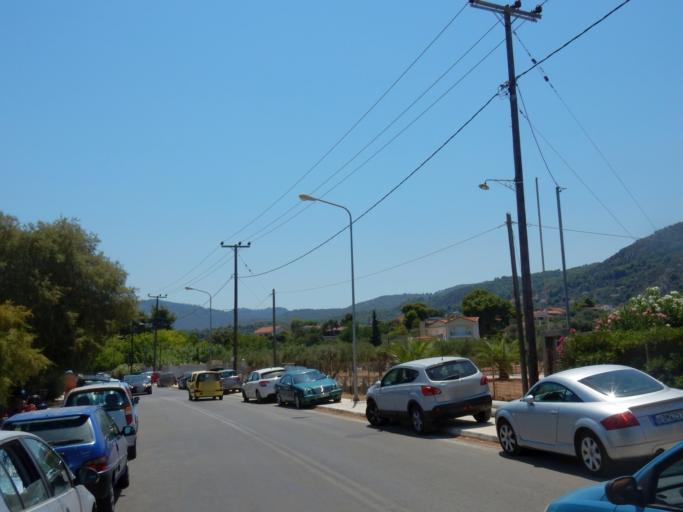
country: GR
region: Attica
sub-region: Nomarchia Anatolikis Attikis
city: Kalamos
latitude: 38.2996
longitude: 23.8796
